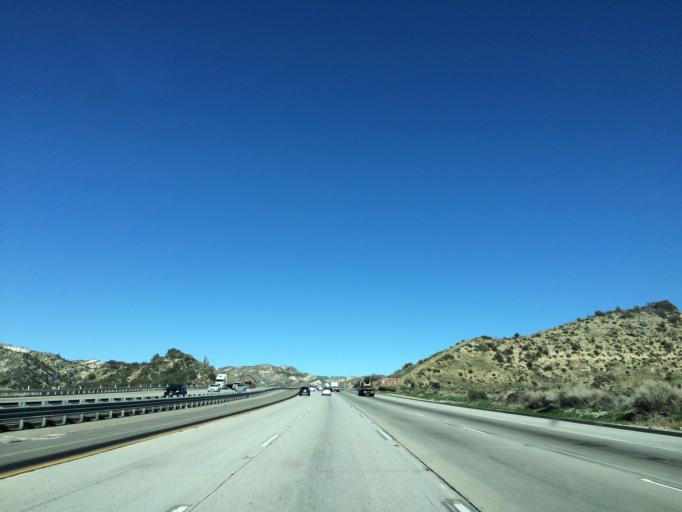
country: US
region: California
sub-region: Kern County
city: Lebec
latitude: 34.7020
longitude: -118.7934
